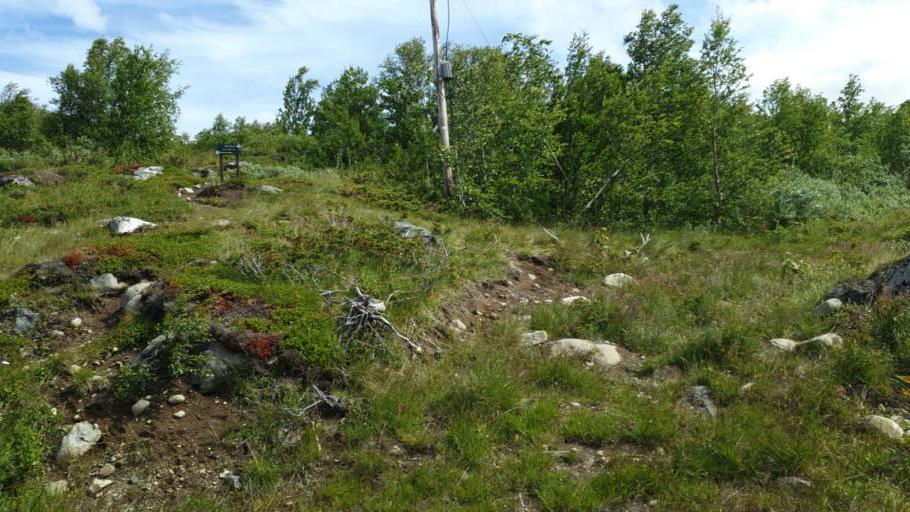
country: NO
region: Oppland
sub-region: Lom
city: Fossbergom
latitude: 61.4934
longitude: 8.8151
